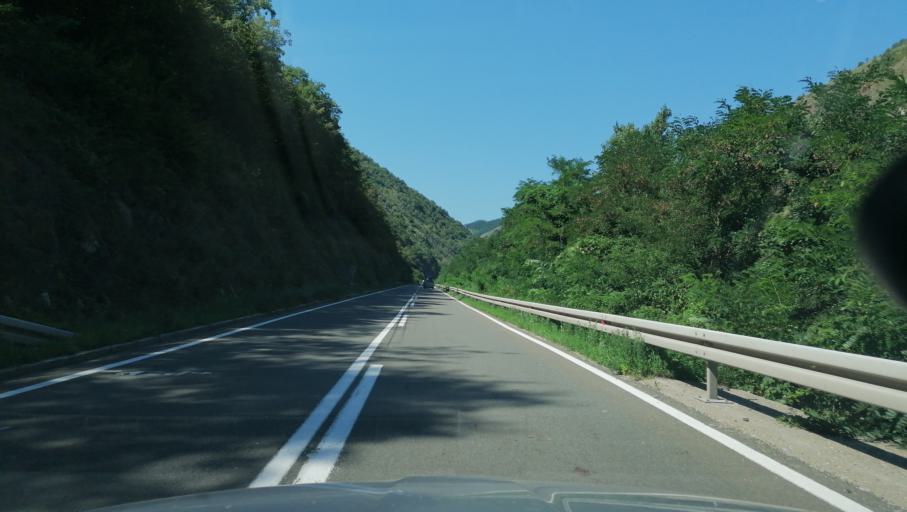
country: RS
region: Central Serbia
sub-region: Raski Okrug
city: Kraljevo
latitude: 43.6034
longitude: 20.5576
